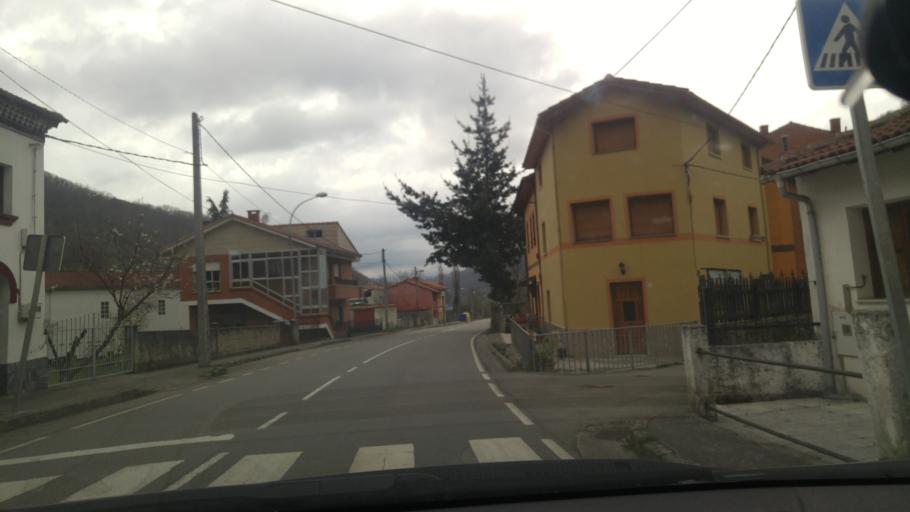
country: ES
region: Asturias
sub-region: Province of Asturias
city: Rio Aller
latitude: 43.1077
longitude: -5.5209
